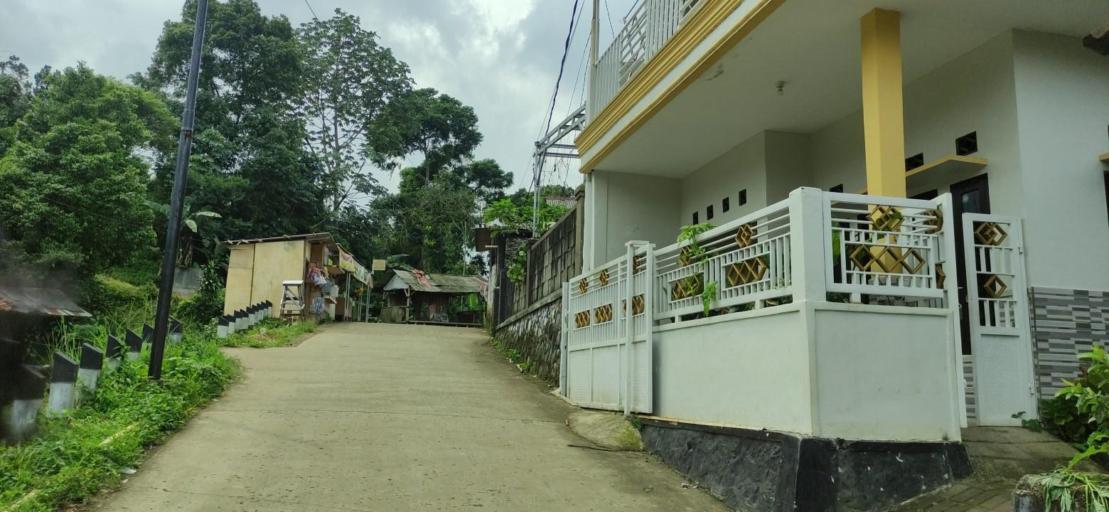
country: ID
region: West Java
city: Caringin
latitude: -6.6434
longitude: 106.8955
